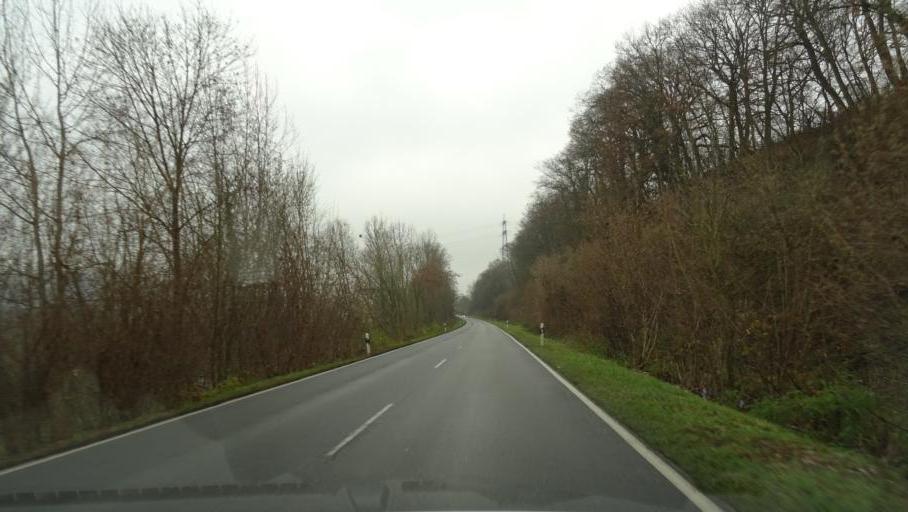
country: DE
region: Baden-Wuerttemberg
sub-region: Karlsruhe Region
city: Neckarzimmern
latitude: 49.3219
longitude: 9.1113
